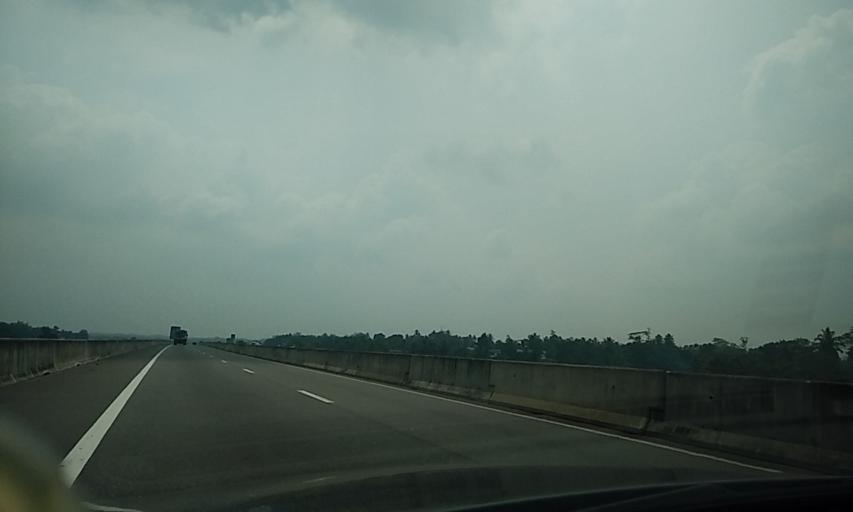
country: LK
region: Western
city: Homagama
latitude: 6.8974
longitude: 79.9790
